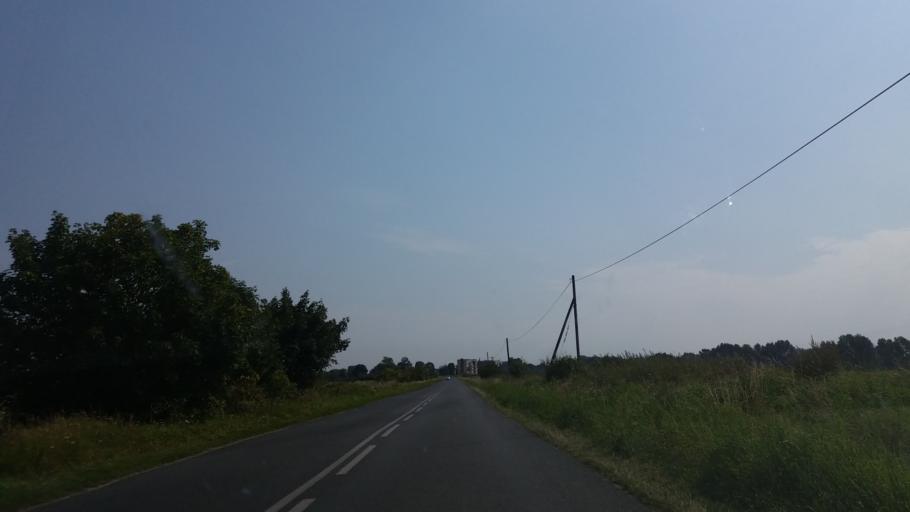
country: PL
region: Lubusz
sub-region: Powiat strzelecko-drezdenecki
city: Strzelce Krajenskie
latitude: 52.9164
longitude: 15.4927
